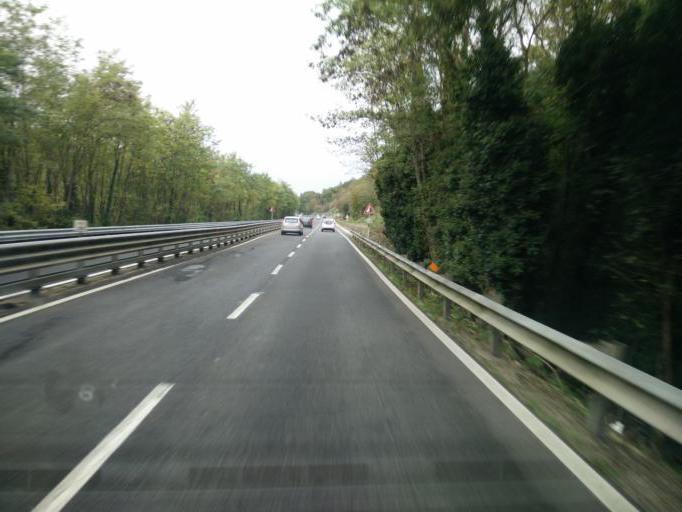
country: IT
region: Tuscany
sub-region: Province of Florence
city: Barberino Val d'Elsa
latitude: 43.5029
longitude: 11.1879
